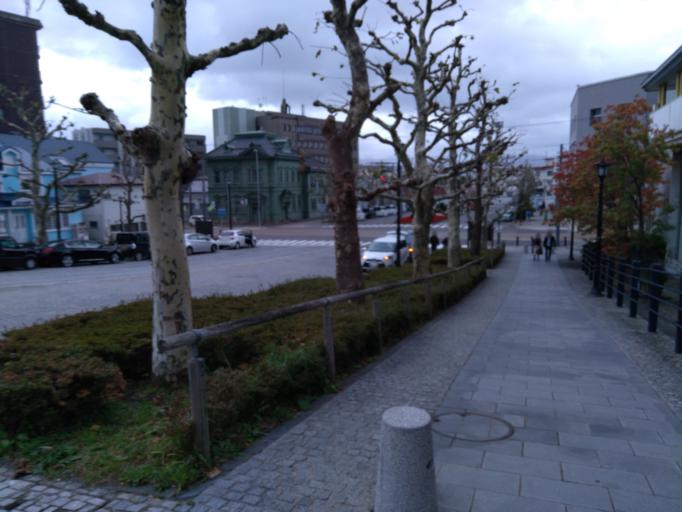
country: JP
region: Hokkaido
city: Hakodate
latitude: 41.7668
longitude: 140.7112
